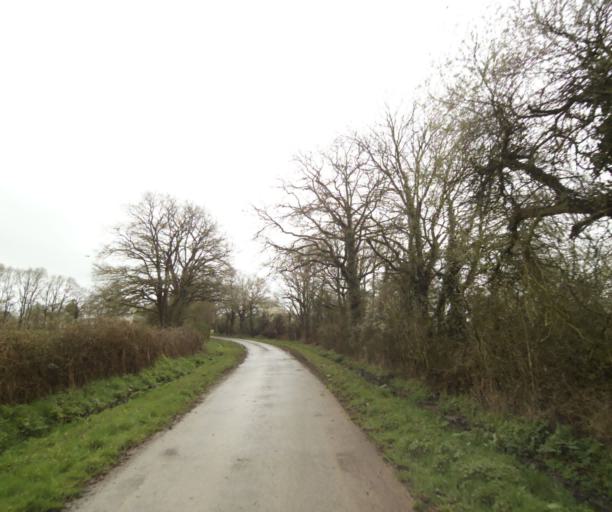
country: FR
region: Pays de la Loire
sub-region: Departement de la Loire-Atlantique
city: Bouvron
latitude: 47.4568
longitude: -1.8921
